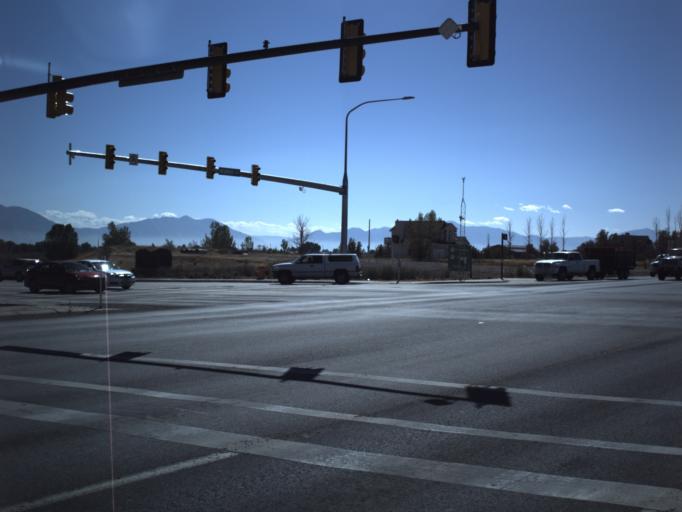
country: US
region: Utah
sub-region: Utah County
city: Saratoga Springs
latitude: 40.3731
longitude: -111.9165
